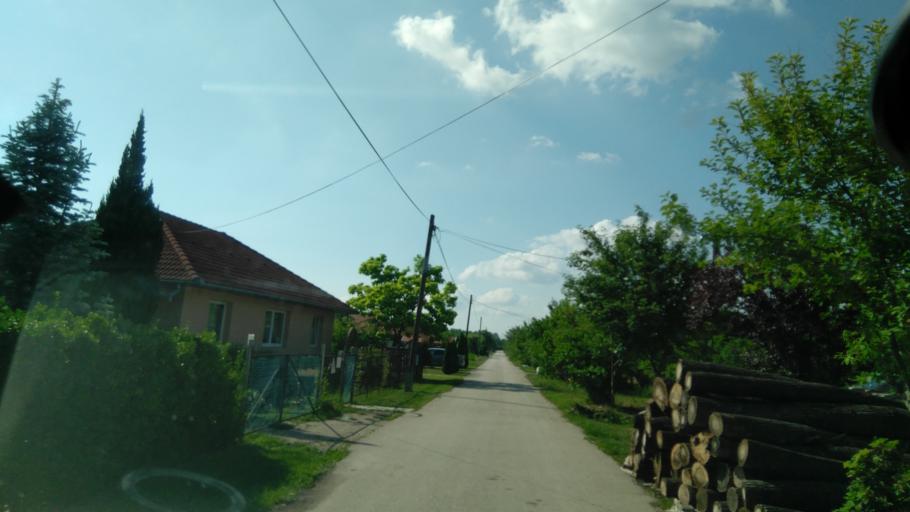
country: HU
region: Bekes
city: Doboz
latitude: 46.7013
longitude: 21.1791
